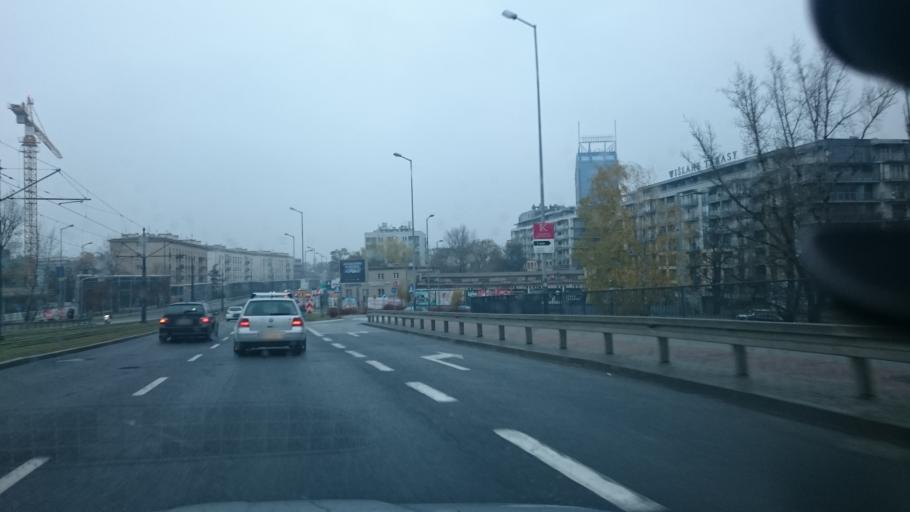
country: PL
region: Lesser Poland Voivodeship
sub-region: Krakow
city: Krakow
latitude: 50.0535
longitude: 19.9605
